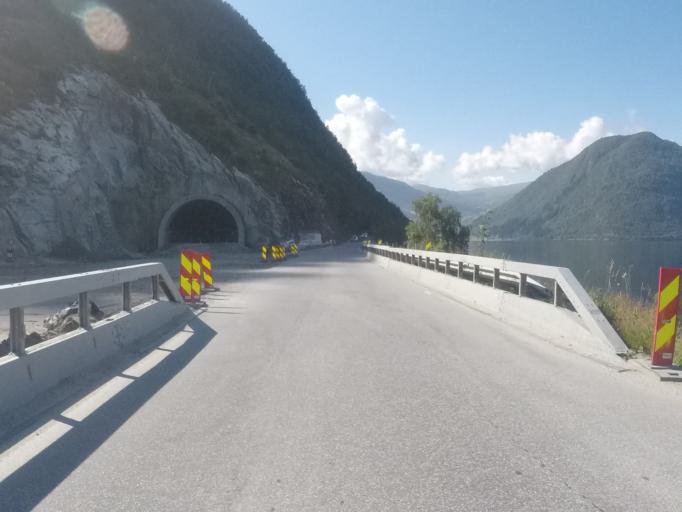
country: NO
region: Sogn og Fjordane
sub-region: Vik
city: Vikoyri
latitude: 61.1179
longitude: 6.6019
